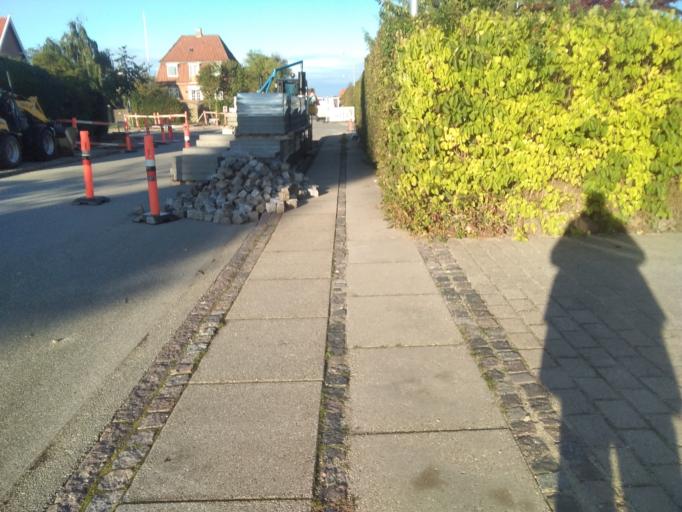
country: DK
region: Capital Region
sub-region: Gladsaxe Municipality
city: Buddinge
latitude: 55.7258
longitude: 12.5071
